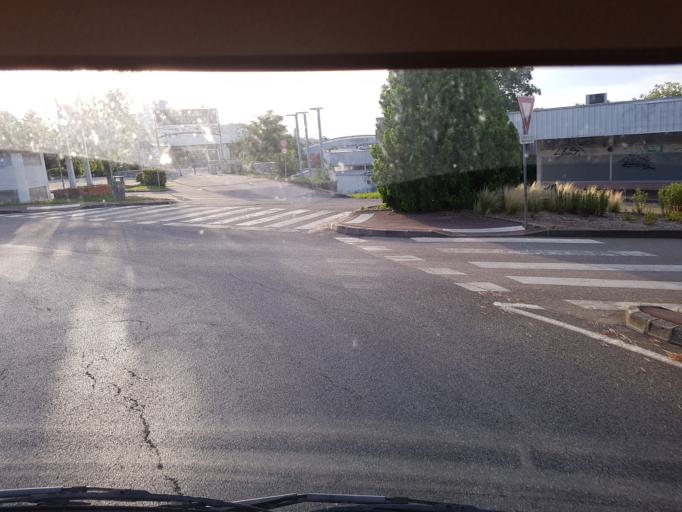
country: FR
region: Rhone-Alpes
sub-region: Departement du Rhone
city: Dardilly
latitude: 45.8207
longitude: 4.7605
